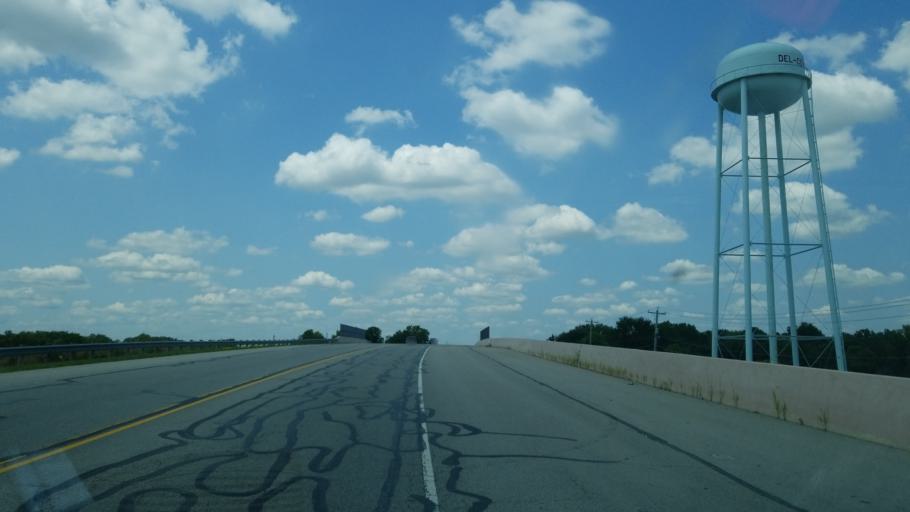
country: US
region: Ohio
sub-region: Delaware County
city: Powell
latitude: 40.1954
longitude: -83.0879
